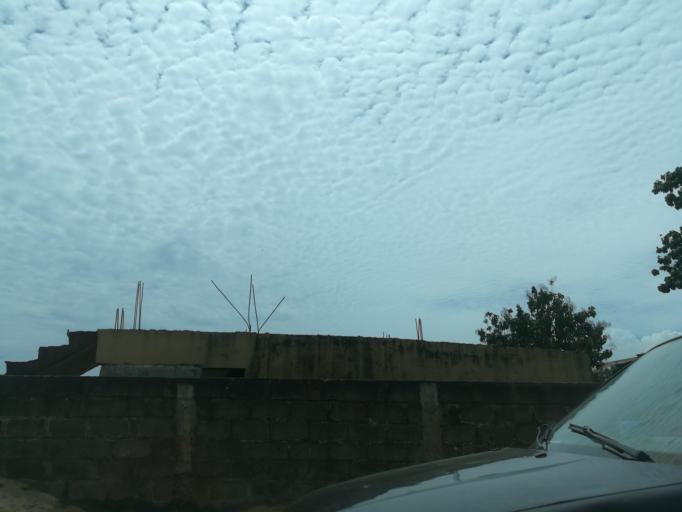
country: NG
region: Lagos
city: Ebute Ikorodu
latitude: 6.5559
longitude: 3.4759
